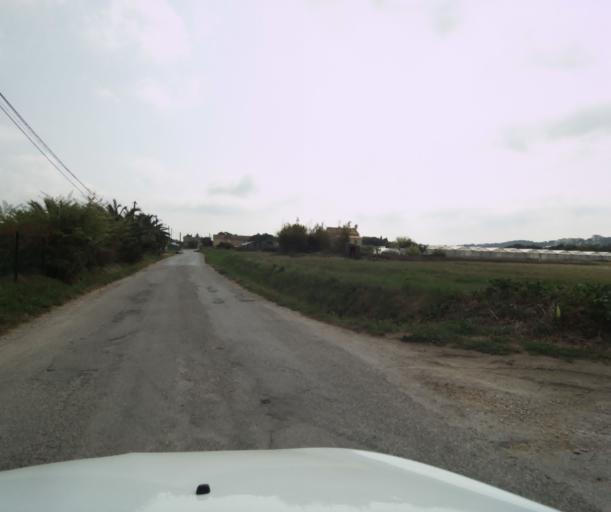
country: FR
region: Provence-Alpes-Cote d'Azur
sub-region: Departement du Var
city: Hyeres
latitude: 43.0915
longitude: 6.1351
